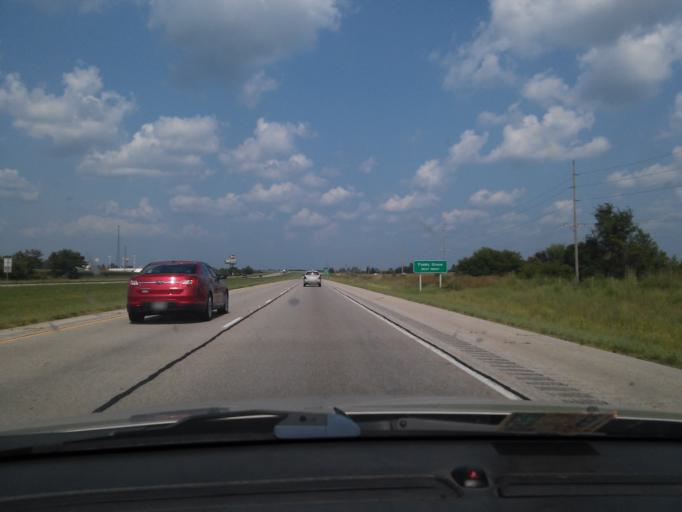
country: US
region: Illinois
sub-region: Logan County
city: Atlanta
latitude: 40.3054
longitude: -89.1759
